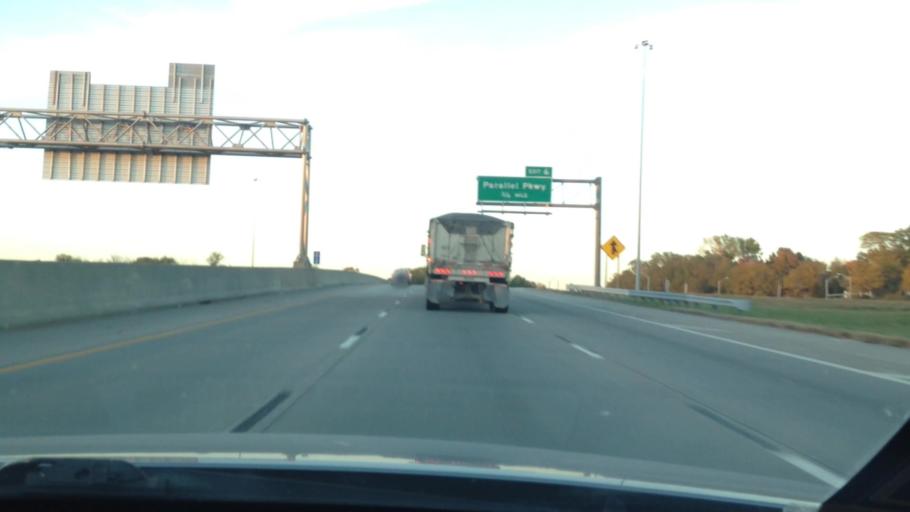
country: US
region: Kansas
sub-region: Wyandotte County
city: Kansas City
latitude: 39.1149
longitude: -94.6820
